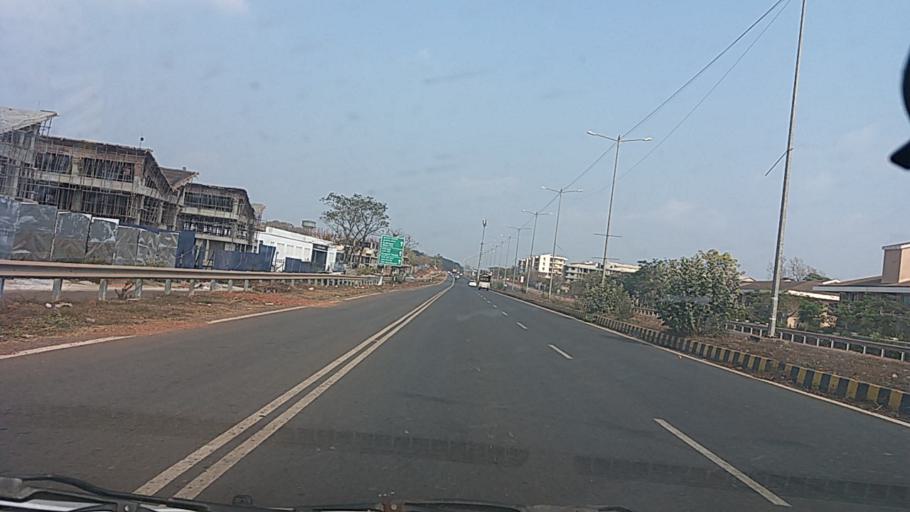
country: IN
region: Goa
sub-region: North Goa
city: Bambolim
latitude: 15.4917
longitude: 73.8889
